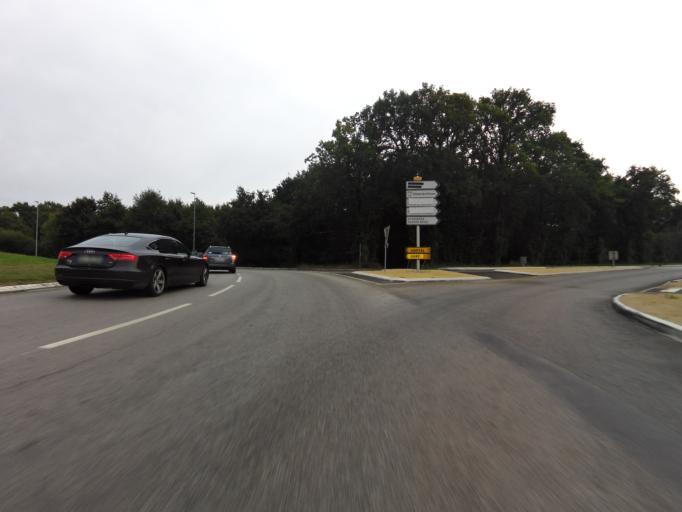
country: FR
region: Brittany
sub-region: Departement du Morbihan
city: Saint-Ave
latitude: 47.6789
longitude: -2.7410
